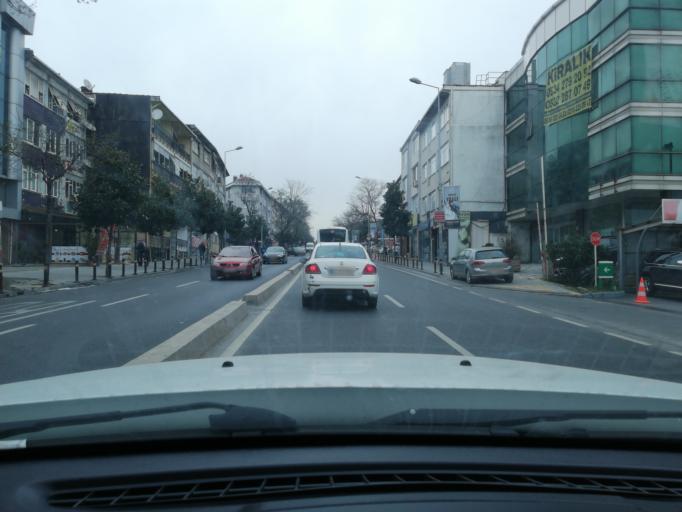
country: TR
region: Istanbul
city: UEskuedar
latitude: 41.0167
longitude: 29.0301
